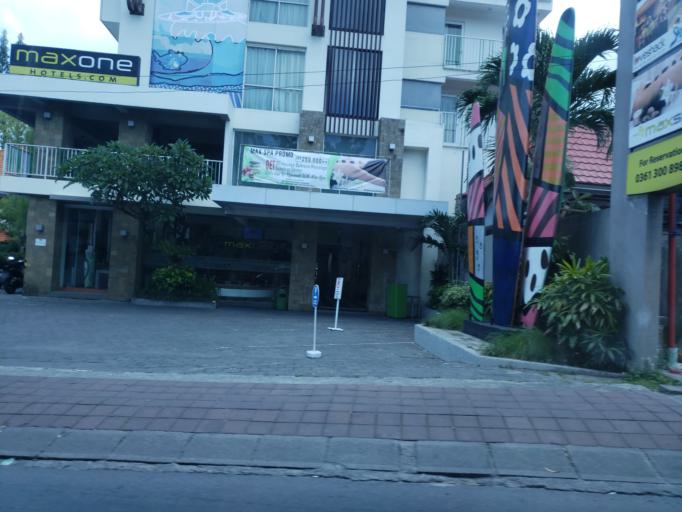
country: ID
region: Bali
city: Jimbaran
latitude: -8.8125
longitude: 115.1574
